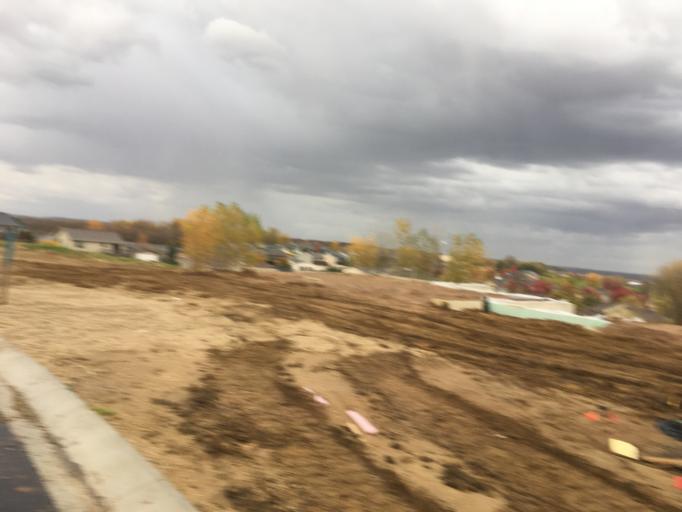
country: US
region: Minnesota
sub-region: Olmsted County
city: Oronoco
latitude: 44.0917
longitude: -92.5246
